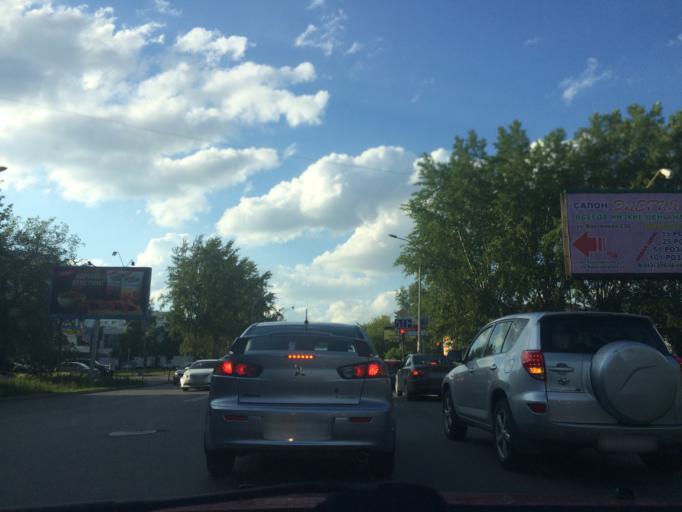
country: RU
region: Sverdlovsk
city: Yekaterinburg
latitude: 56.8206
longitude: 60.6397
